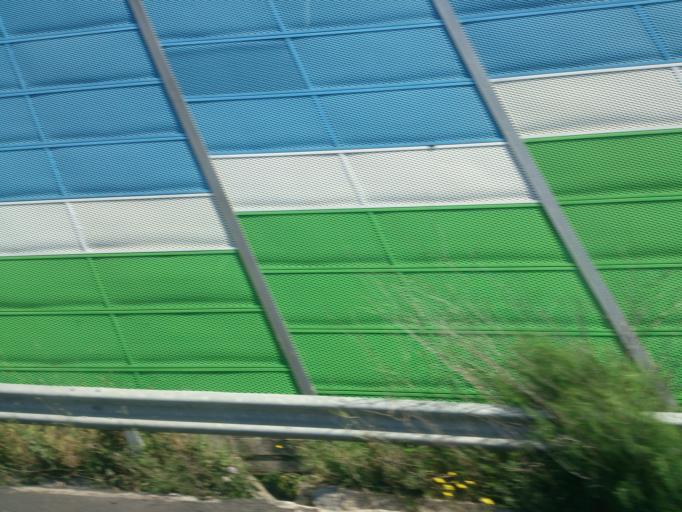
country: PT
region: Lisbon
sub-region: Mafra
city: Malveira
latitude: 38.9360
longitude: -9.2902
